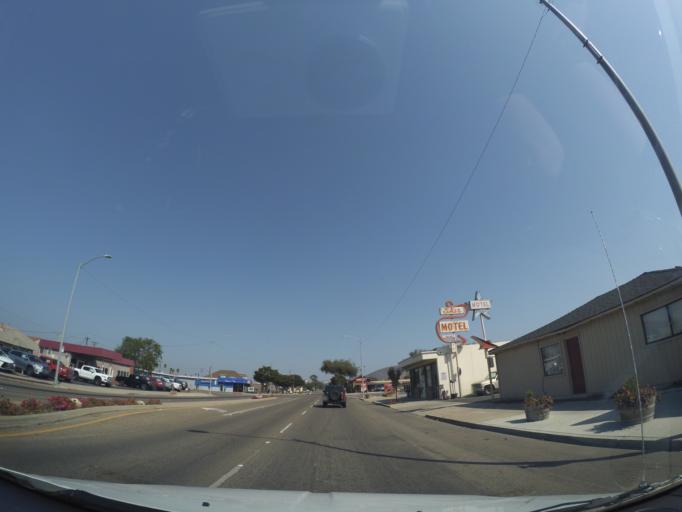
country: US
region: California
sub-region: Santa Barbara County
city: Lompoc
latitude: 34.6389
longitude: -120.4560
